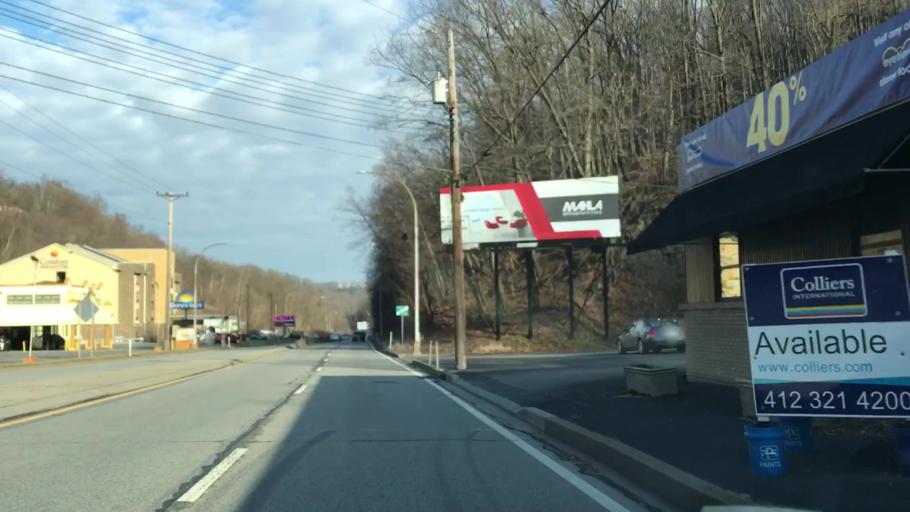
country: US
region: Pennsylvania
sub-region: Allegheny County
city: Green Tree
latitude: 40.4184
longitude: -80.0297
